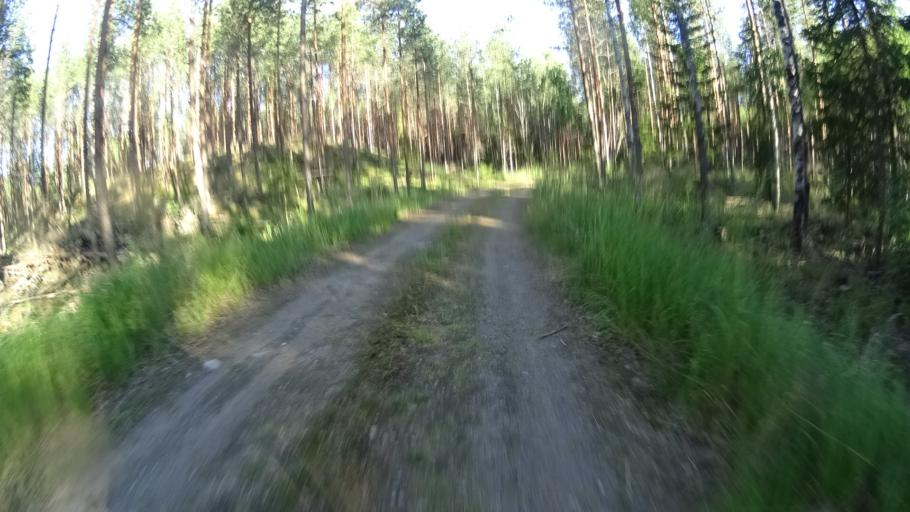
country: FI
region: Uusimaa
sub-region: Helsinki
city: Karkkila
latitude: 60.6644
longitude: 24.1318
